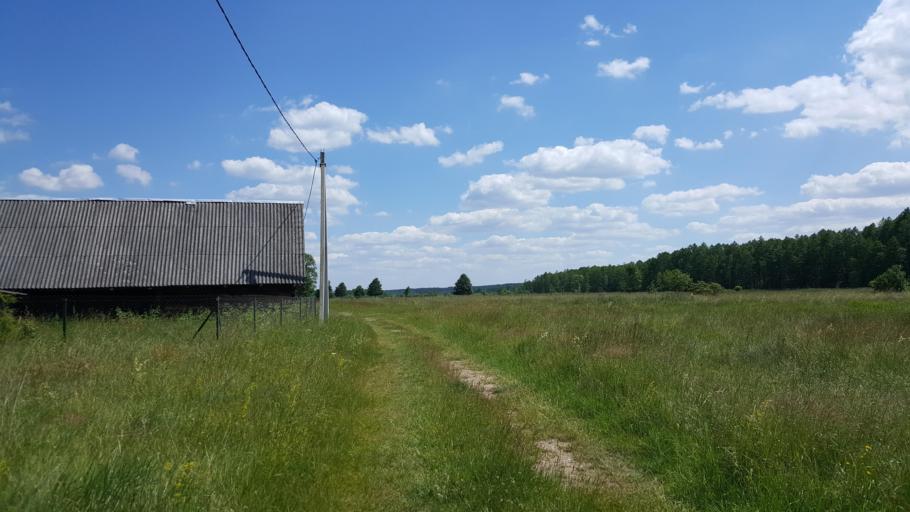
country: BY
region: Brest
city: Kamyanyuki
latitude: 52.5799
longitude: 23.7491
